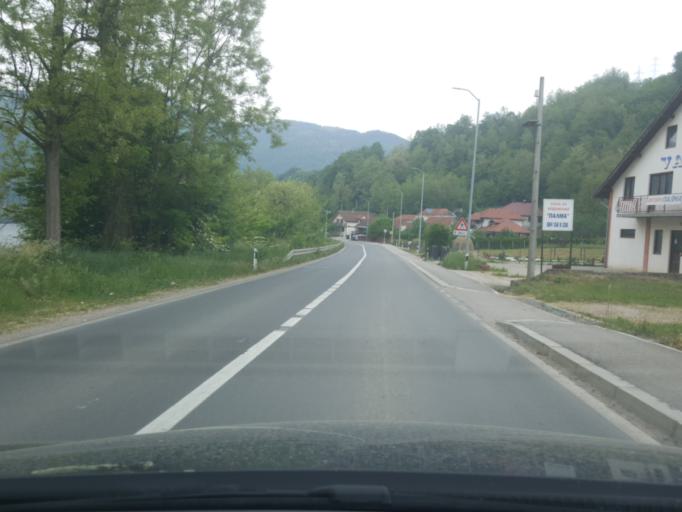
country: RS
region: Central Serbia
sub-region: Zlatiborski Okrug
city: Bajina Basta
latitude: 43.9879
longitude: 19.5691
